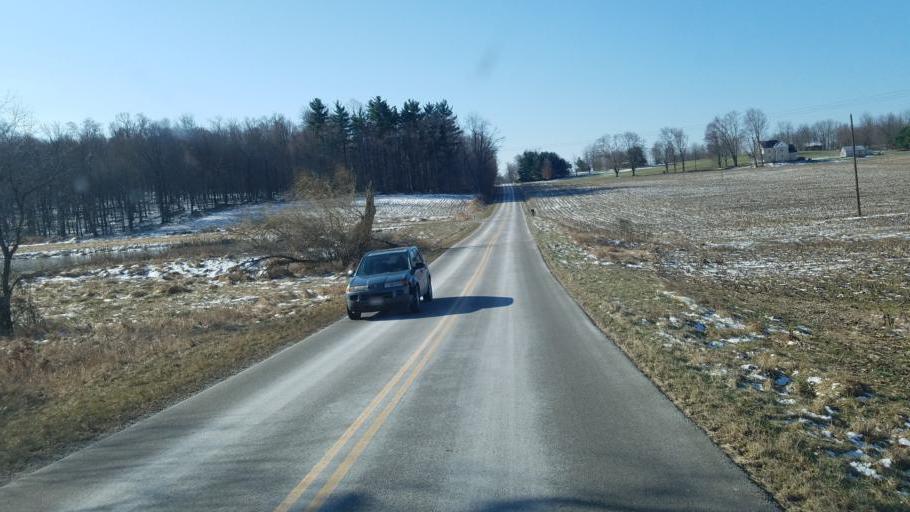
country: US
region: Ohio
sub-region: Knox County
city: Fredericktown
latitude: 40.4650
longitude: -82.4846
